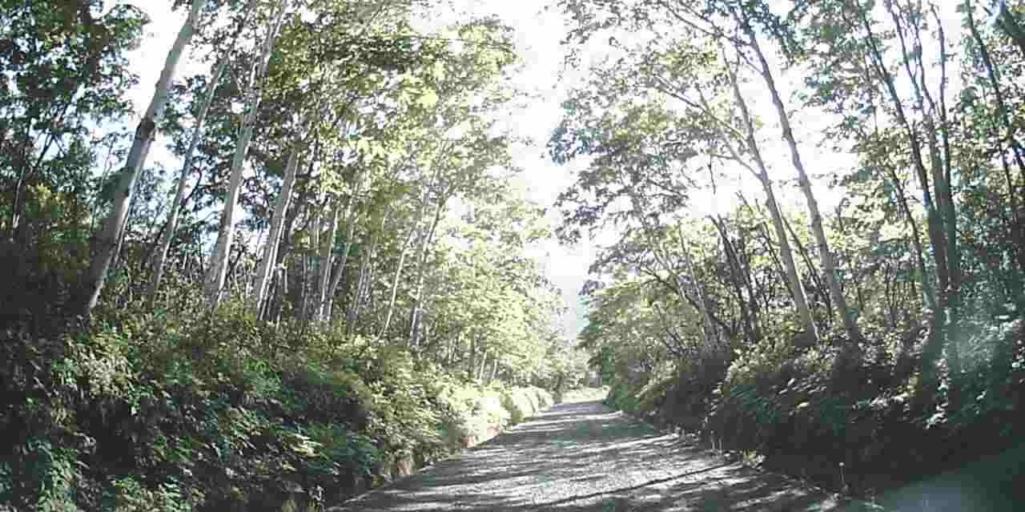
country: JP
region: Hokkaido
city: Shiraoi
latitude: 42.7033
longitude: 141.3935
